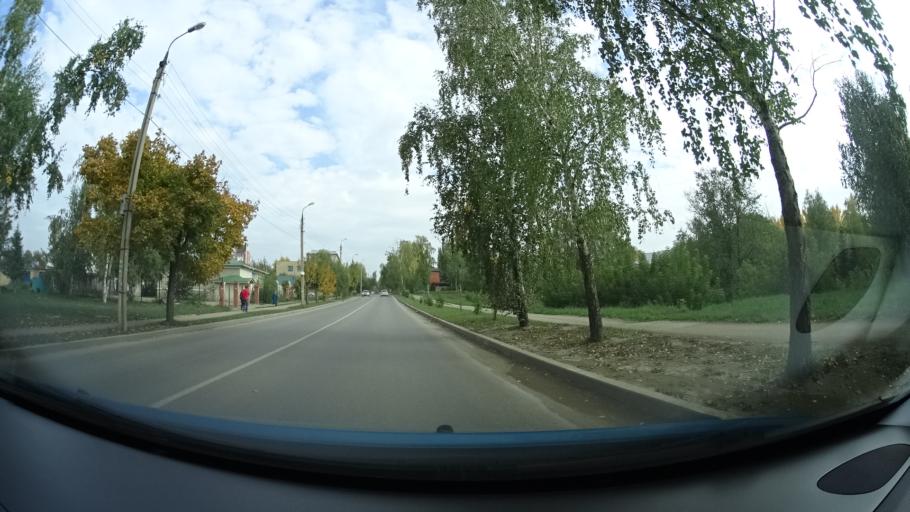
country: RU
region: Bashkortostan
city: Oktyabr'skiy
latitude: 54.4890
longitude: 53.4622
